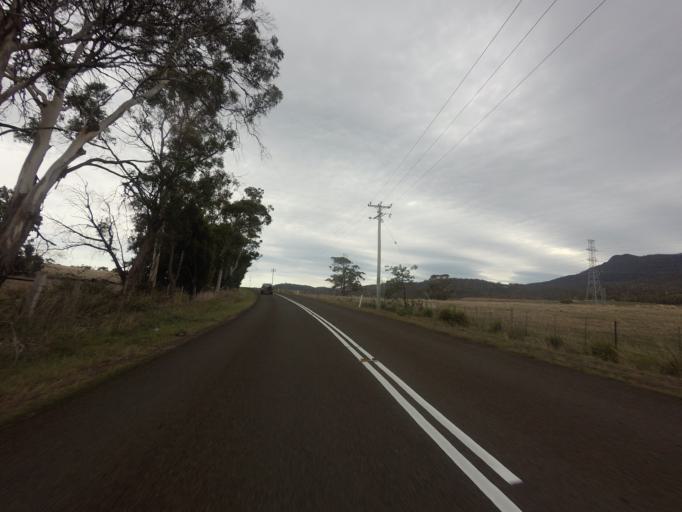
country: AU
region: Tasmania
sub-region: Brighton
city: Bridgewater
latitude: -42.6660
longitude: 147.1328
